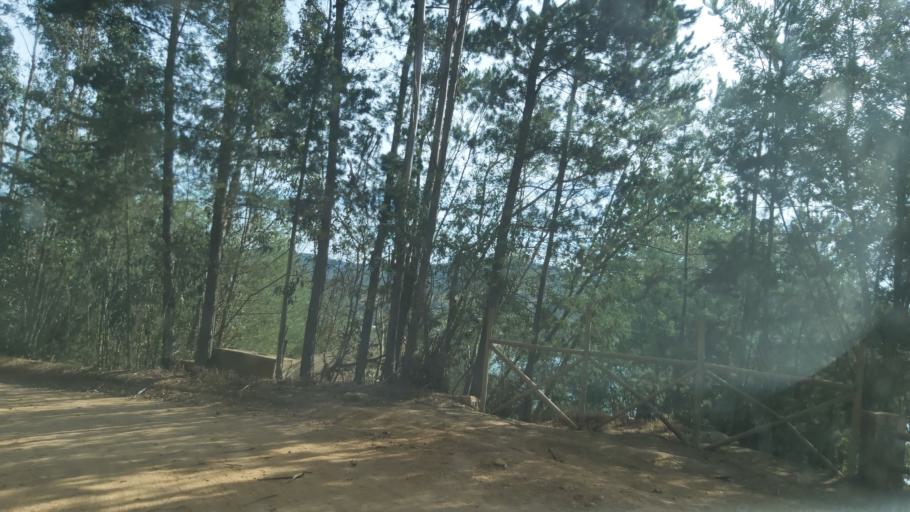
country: CL
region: Maule
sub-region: Provincia de Talca
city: Constitucion
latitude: -34.8436
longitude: -72.0403
